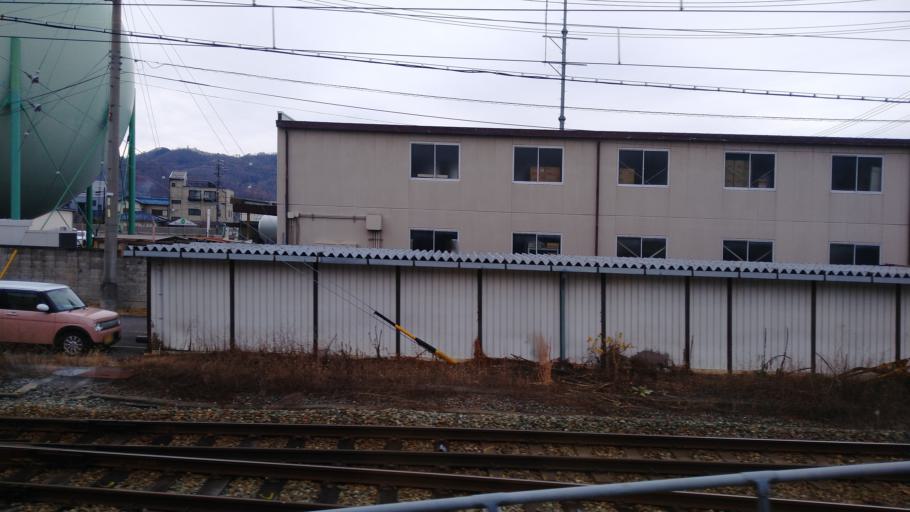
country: JP
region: Nagano
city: Ueda
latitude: 36.3949
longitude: 138.2512
